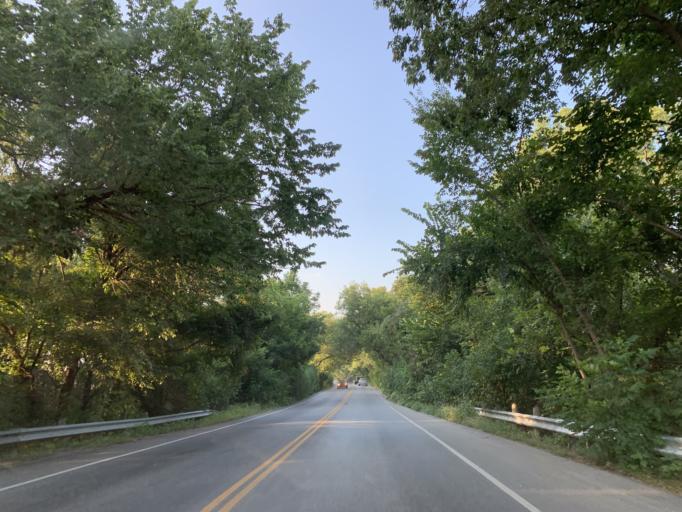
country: US
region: Texas
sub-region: Tarrant County
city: Hurst
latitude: 32.7822
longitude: -97.1783
